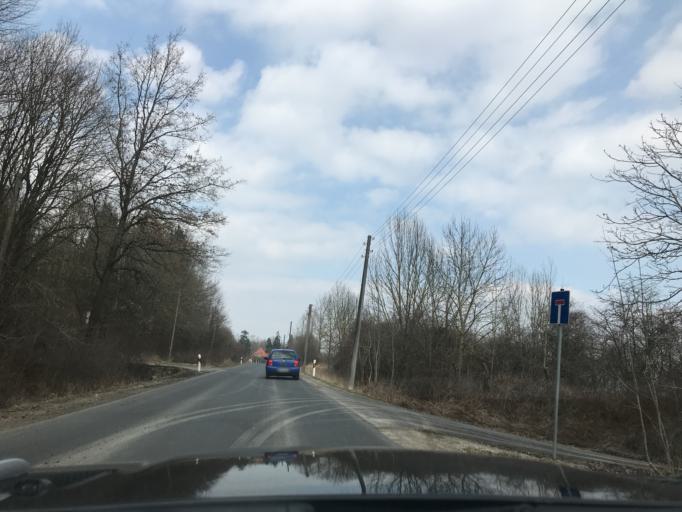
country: DE
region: Thuringia
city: Oberdorla
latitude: 51.1919
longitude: 10.3943
